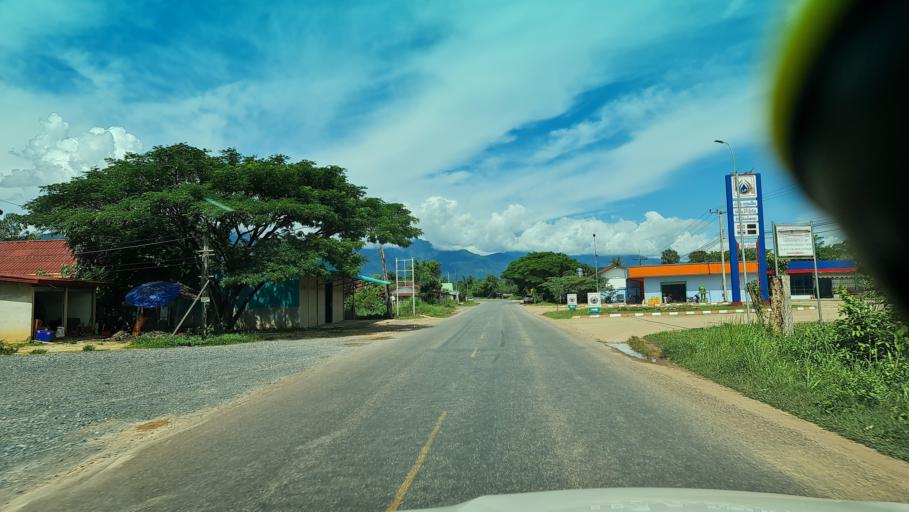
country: LA
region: Bolikhamxai
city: Pakkading
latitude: 18.2991
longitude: 104.1041
